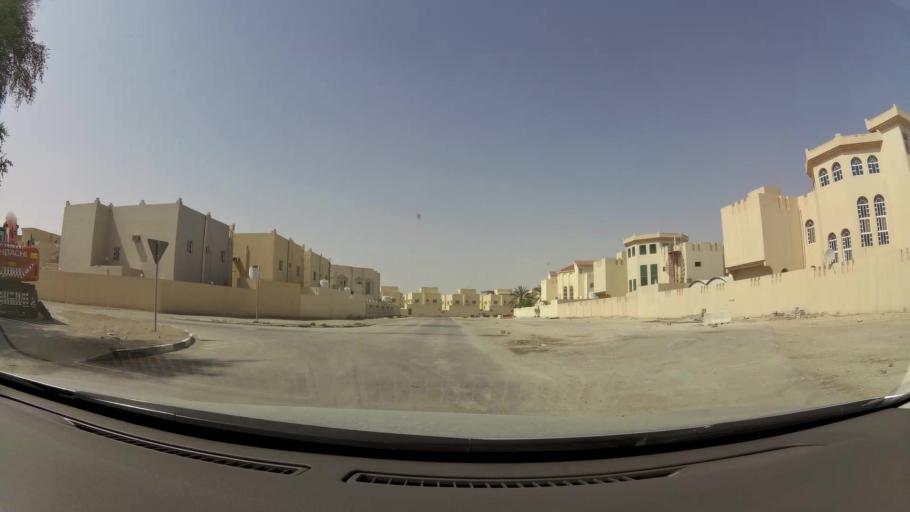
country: QA
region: Baladiyat Umm Salal
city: Umm Salal Muhammad
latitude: 25.3659
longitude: 51.4433
